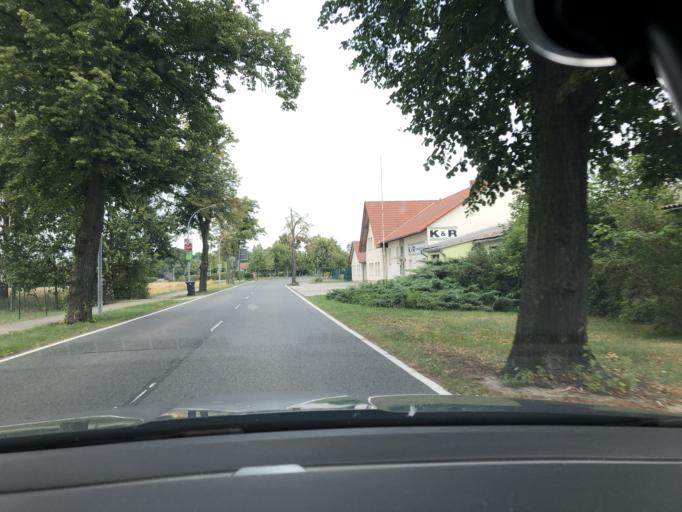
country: DE
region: Brandenburg
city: Kasel-Golzig
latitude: 51.9601
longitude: 13.7454
